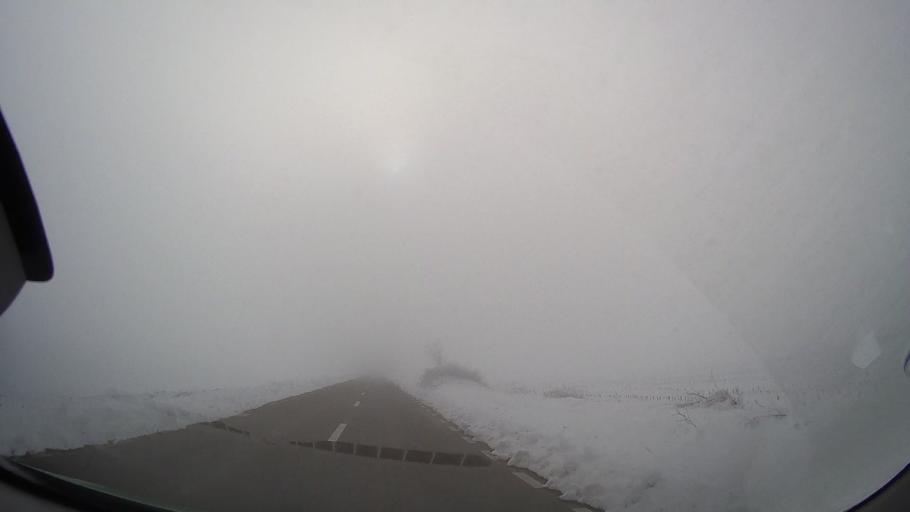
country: RO
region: Iasi
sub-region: Comuna Valea Seaca
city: Valea Seaca
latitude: 47.2784
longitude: 26.6706
